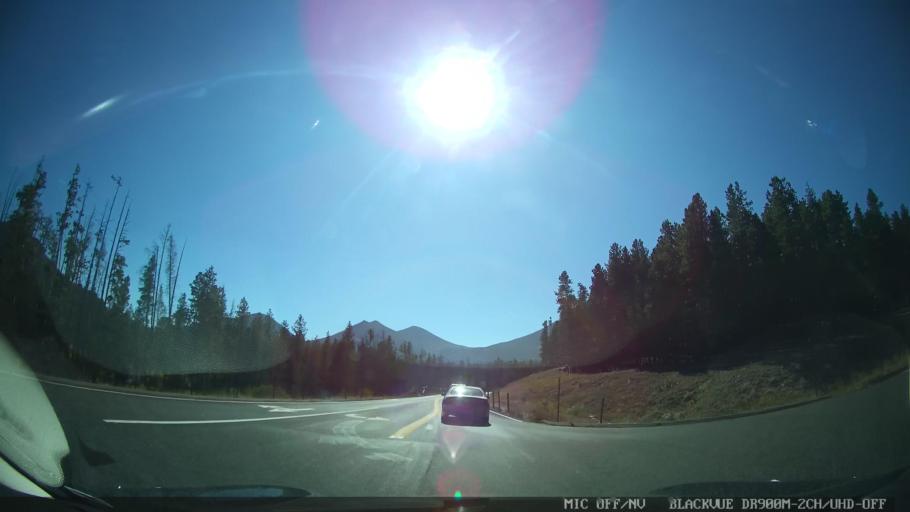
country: US
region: Colorado
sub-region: Larimer County
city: Estes Park
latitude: 40.3300
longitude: -105.6000
